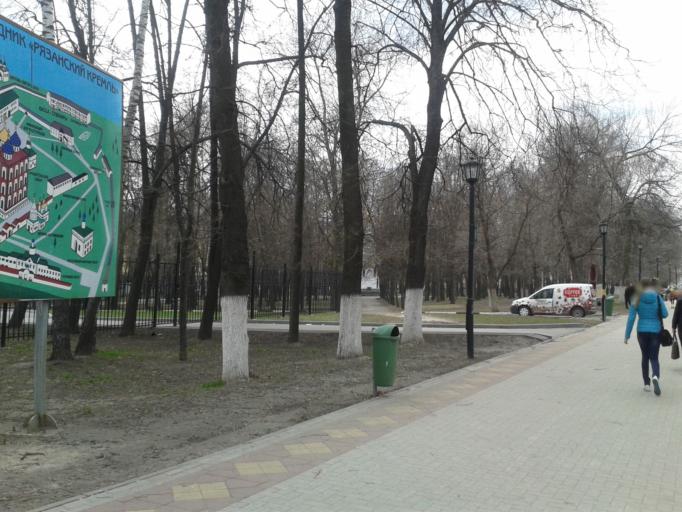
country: RU
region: Rjazan
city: Ryazan'
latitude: 54.6346
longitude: 39.7463
